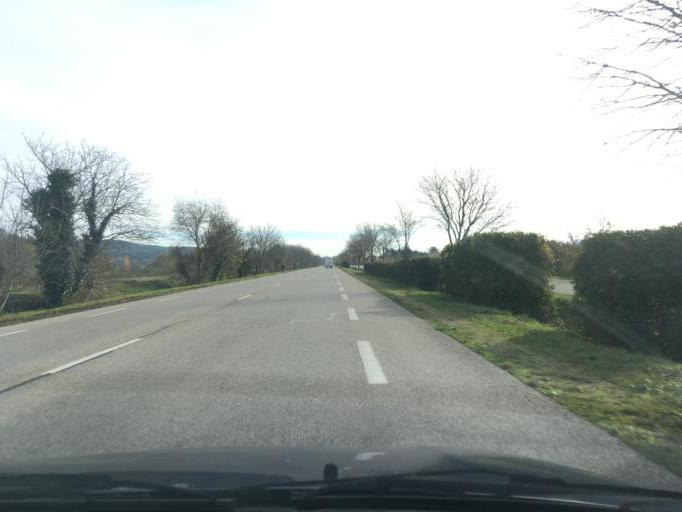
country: FR
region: Provence-Alpes-Cote d'Azur
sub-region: Departement du Vaucluse
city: Cadenet
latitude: 43.7335
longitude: 5.3528
